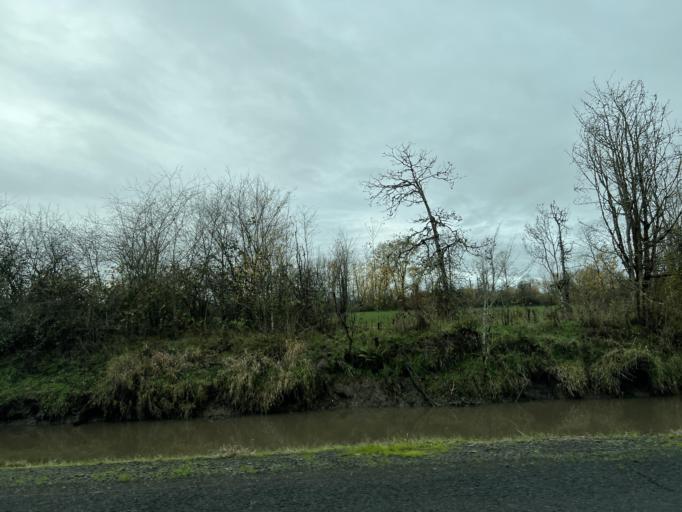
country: US
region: Oregon
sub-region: Marion County
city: Jefferson
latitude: 44.7996
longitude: -123.0872
